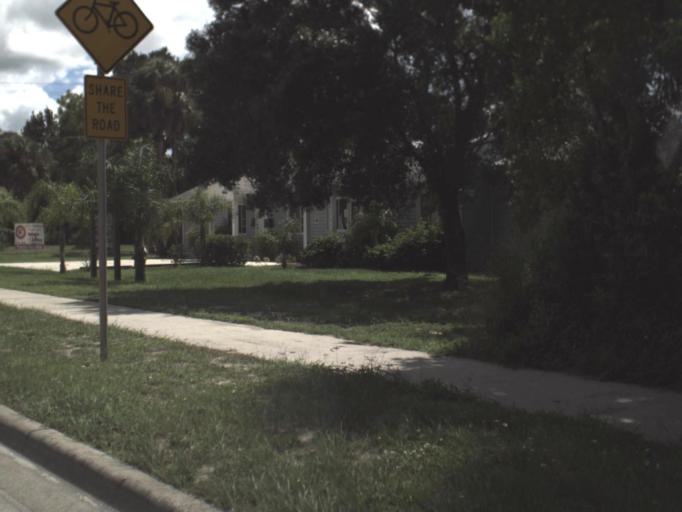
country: US
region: Florida
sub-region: DeSoto County
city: Arcadia
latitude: 27.2134
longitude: -81.8579
